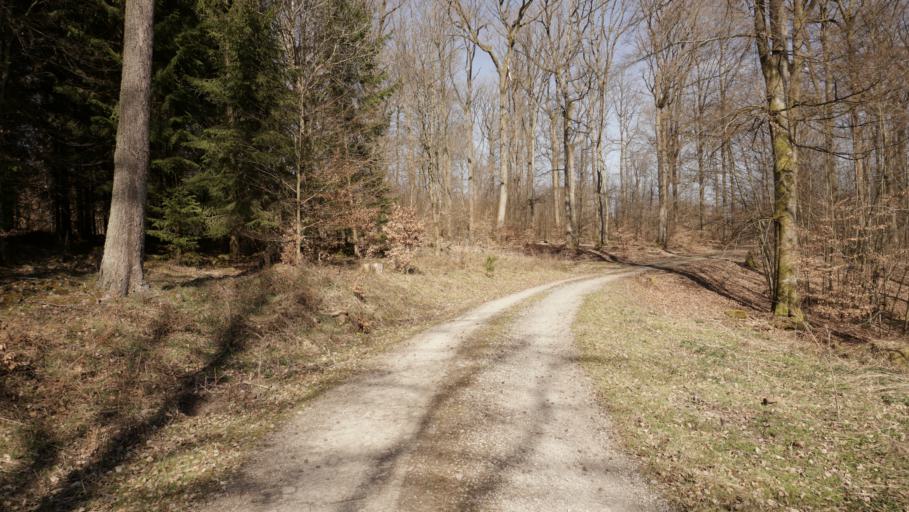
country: DE
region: Baden-Wuerttemberg
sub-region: Karlsruhe Region
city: Fahrenbach
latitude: 49.4370
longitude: 9.1226
